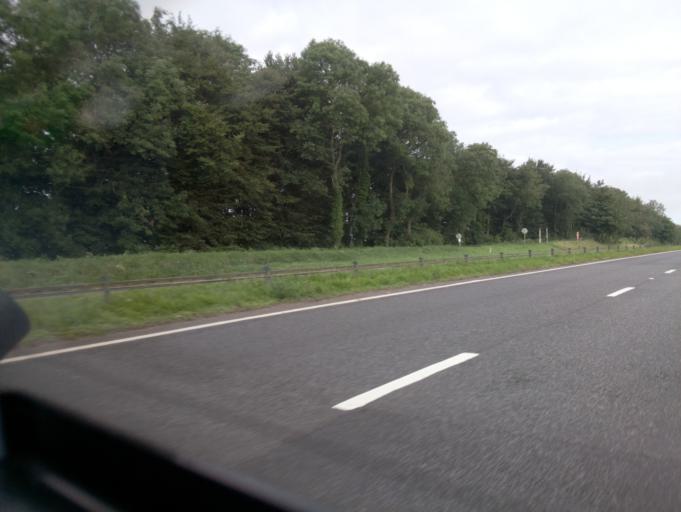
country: GB
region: England
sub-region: Gloucestershire
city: Charlton Kings
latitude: 51.8034
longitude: -2.0578
